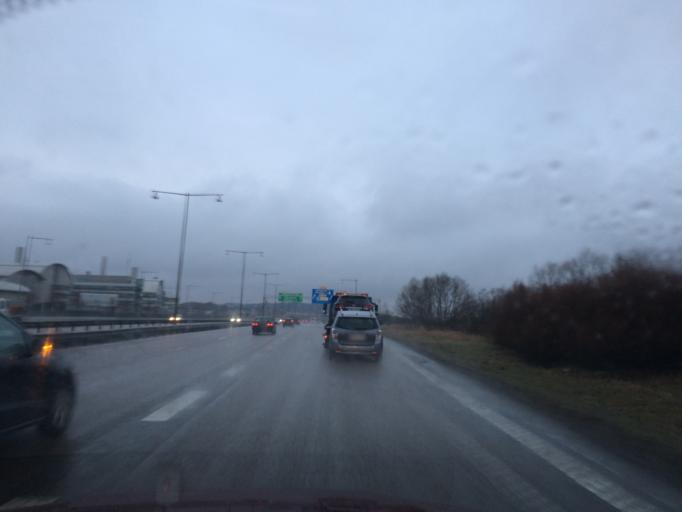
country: SE
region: Vaestra Goetaland
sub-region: Molndal
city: Moelndal
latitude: 57.6419
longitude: 12.0268
